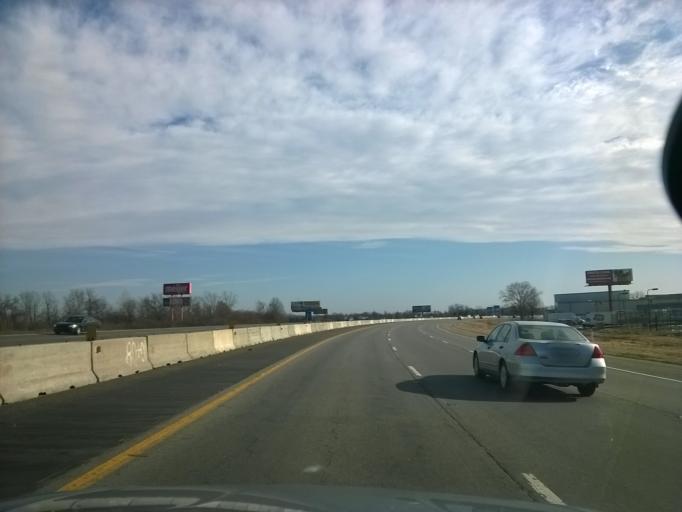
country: US
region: Indiana
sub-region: Marion County
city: Southport
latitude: 39.6566
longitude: -86.0769
